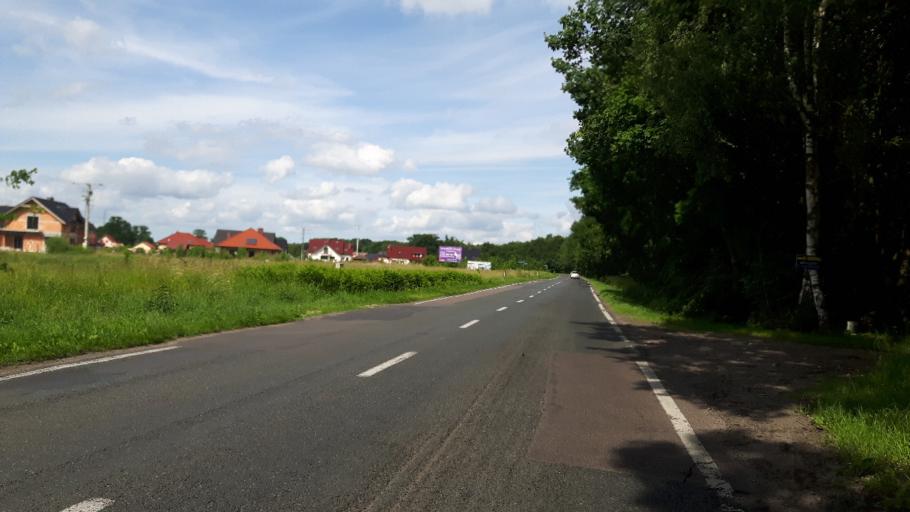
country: PL
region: West Pomeranian Voivodeship
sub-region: Powiat gryfinski
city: Stare Czarnowo
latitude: 53.4291
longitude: 14.7234
